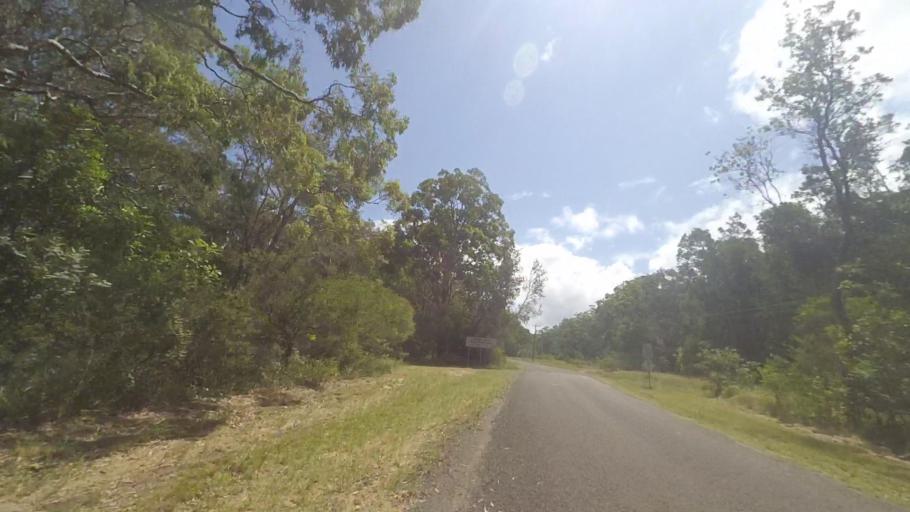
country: AU
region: New South Wales
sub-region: Great Lakes
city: Bulahdelah
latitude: -32.5089
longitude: 152.2972
